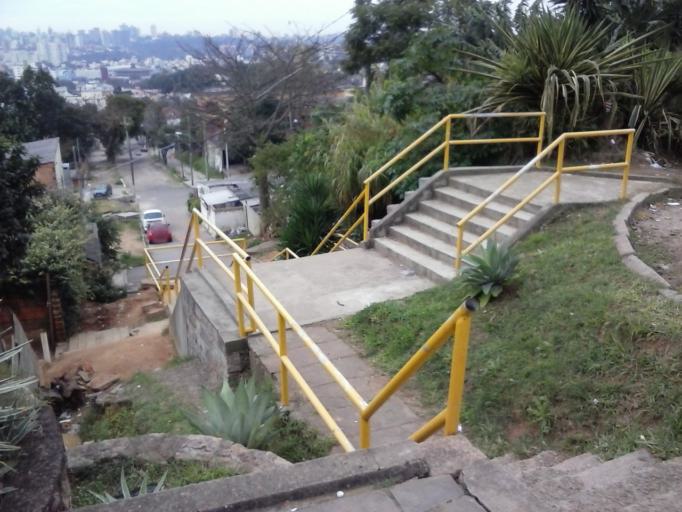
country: BR
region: Rio Grande do Sul
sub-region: Porto Alegre
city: Porto Alegre
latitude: -30.0639
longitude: -51.1943
